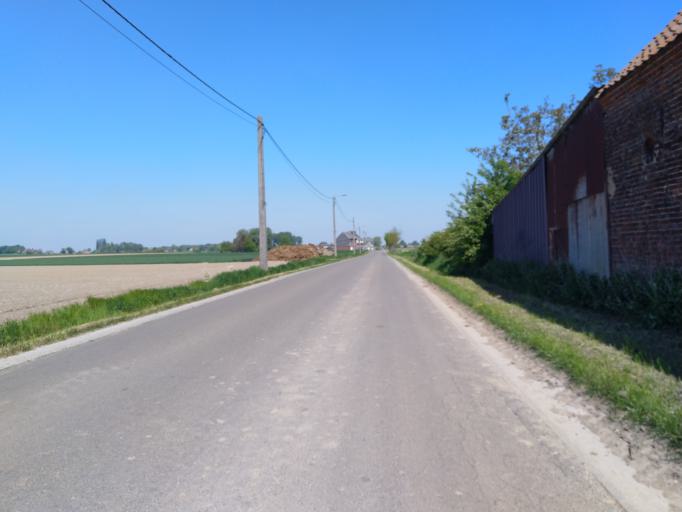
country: BE
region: Wallonia
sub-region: Province du Hainaut
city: Soignies
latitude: 50.5699
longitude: 3.9869
